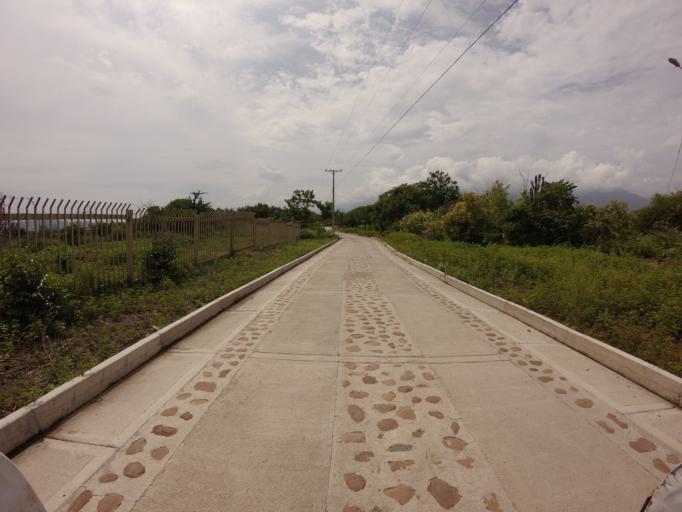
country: CO
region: Tolima
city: Natagaima
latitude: 3.4596
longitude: -75.1407
